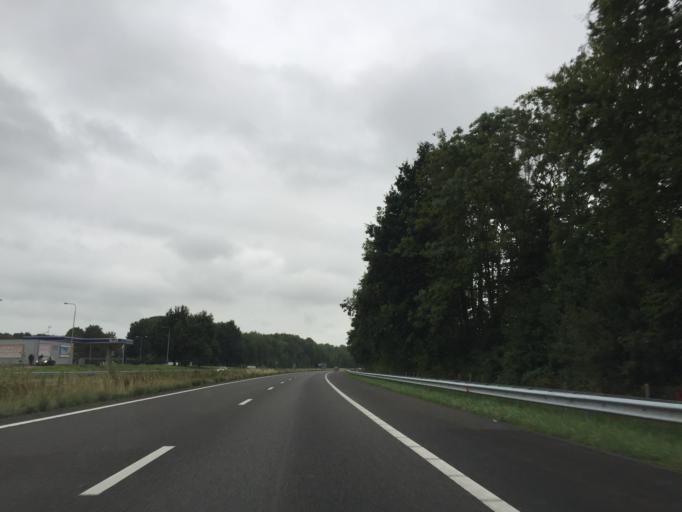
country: NL
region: Limburg
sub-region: Eijsden-Margraten
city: Eijsden
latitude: 50.7785
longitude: 5.7291
